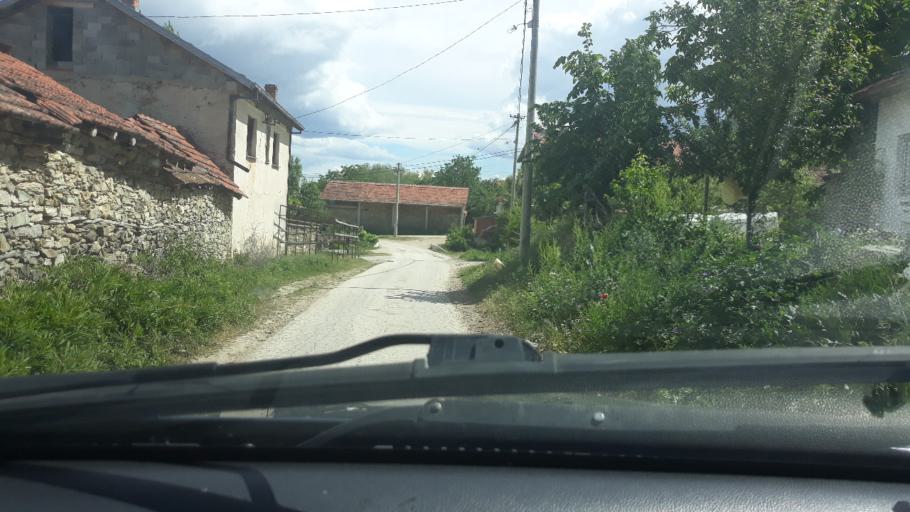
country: MK
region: Krivogastani
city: Krivogashtani
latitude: 41.3224
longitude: 21.3045
